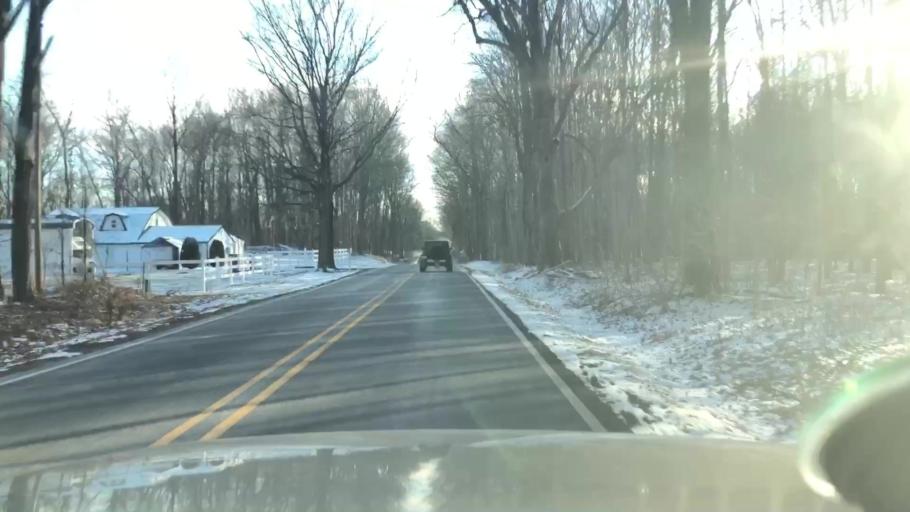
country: US
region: Michigan
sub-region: Jackson County
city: Vandercook Lake
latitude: 42.1114
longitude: -84.4513
